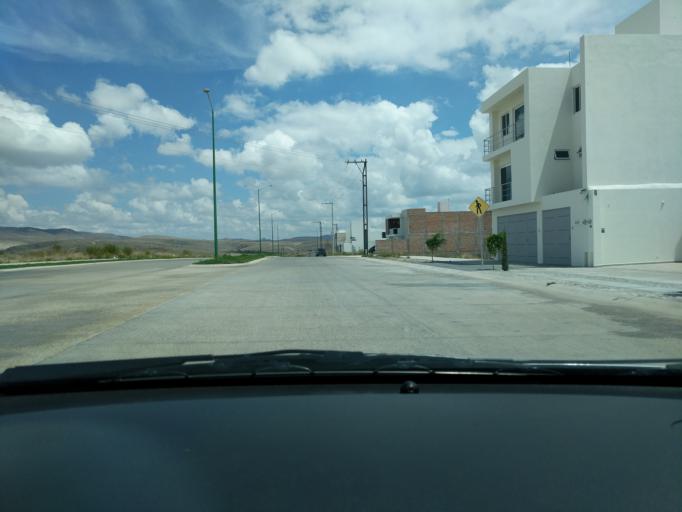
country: MX
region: San Luis Potosi
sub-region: Mexquitic de Carmona
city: Guadalupe Victoria
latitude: 22.1591
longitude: -101.0548
